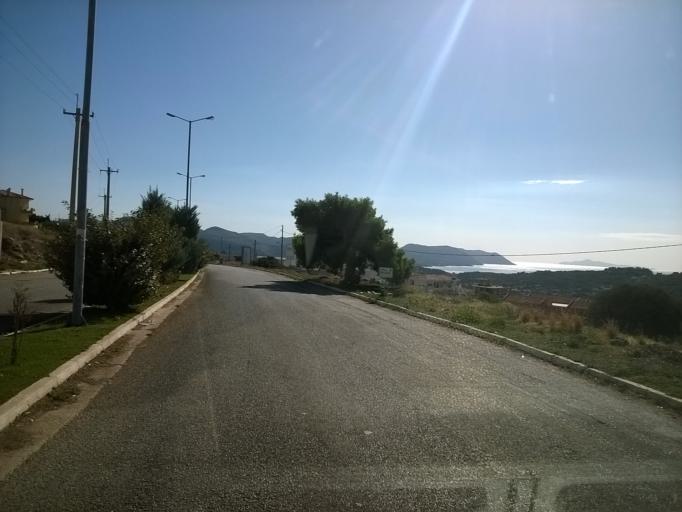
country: GR
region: Attica
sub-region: Nomarchia Anatolikis Attikis
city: Saronida
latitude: 37.7431
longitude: 23.9225
